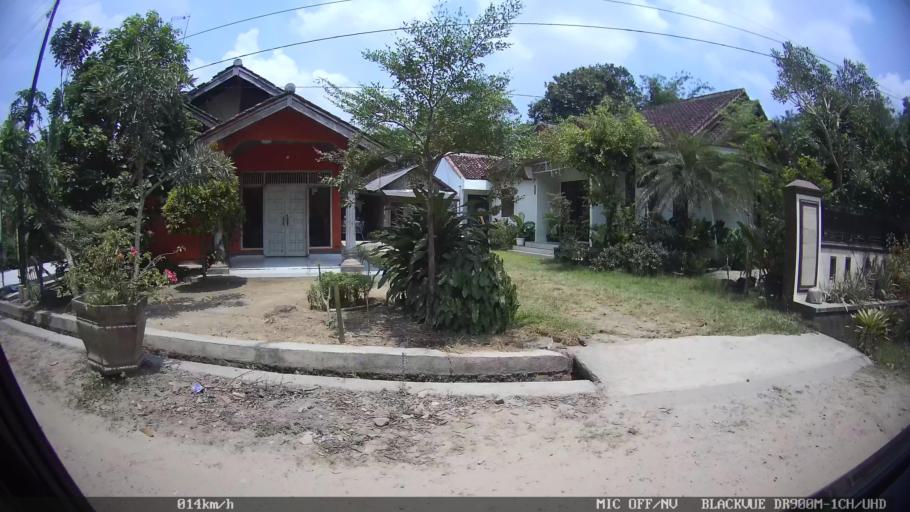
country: ID
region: Lampung
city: Pringsewu
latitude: -5.3441
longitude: 104.9860
